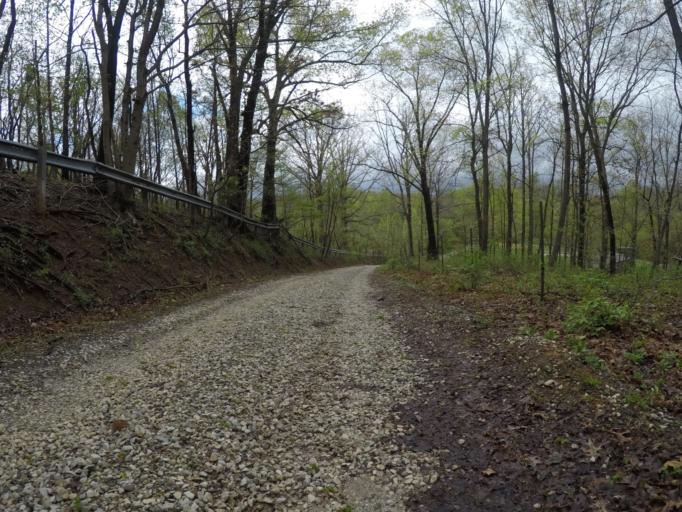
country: US
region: West Virginia
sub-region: Cabell County
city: Huntington
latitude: 38.3884
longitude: -82.4811
